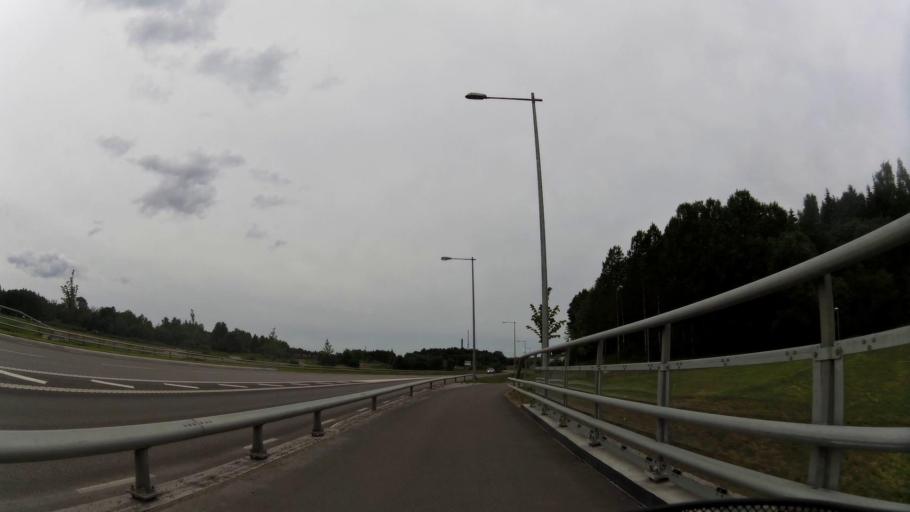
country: SE
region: OEstergoetland
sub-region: Linkopings Kommun
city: Linkoping
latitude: 58.3882
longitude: 15.5897
